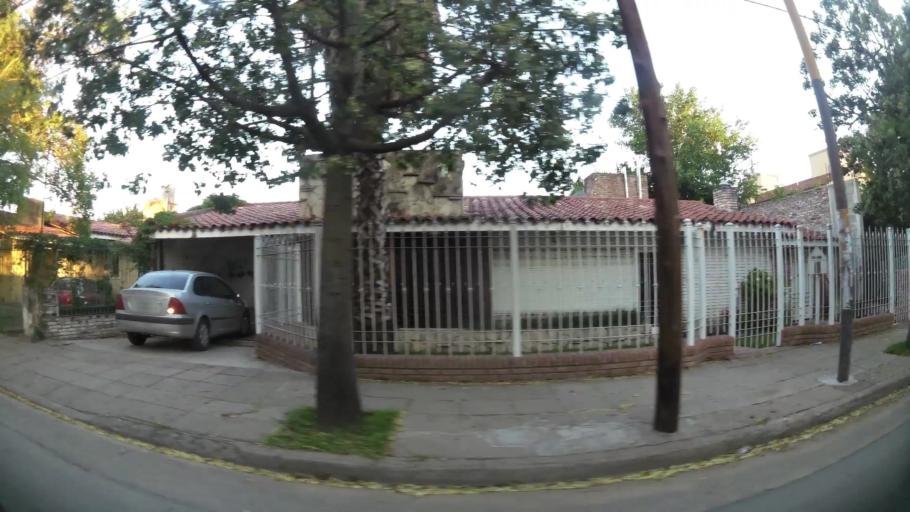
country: AR
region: Cordoba
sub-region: Departamento de Capital
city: Cordoba
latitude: -31.3750
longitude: -64.2225
